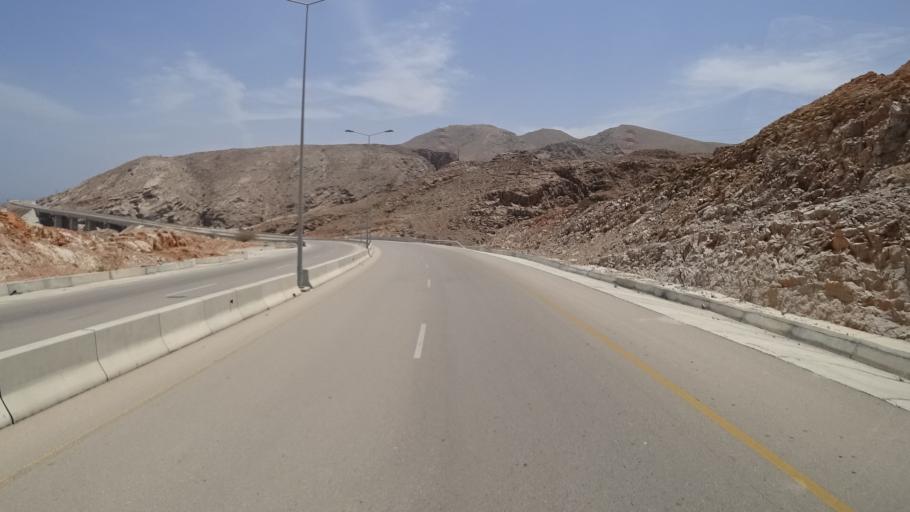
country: OM
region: Ash Sharqiyah
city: Sur
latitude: 22.6984
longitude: 59.3645
